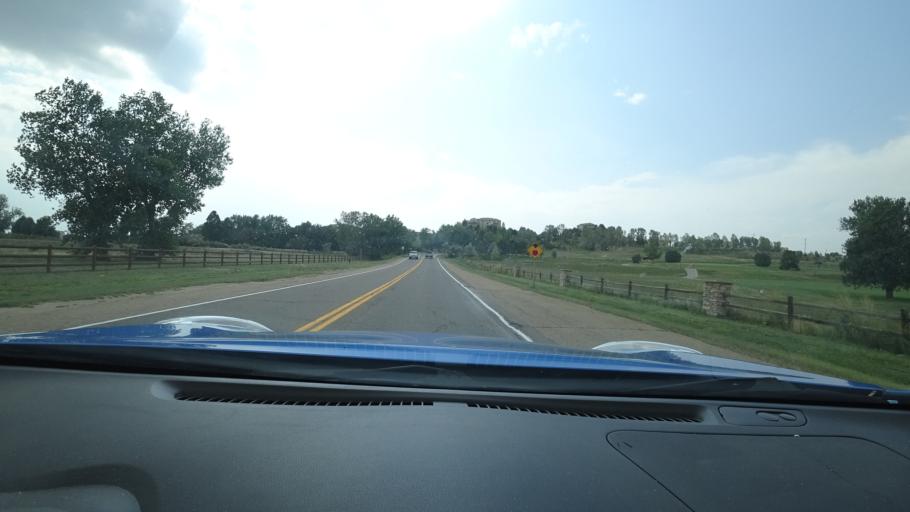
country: US
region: Colorado
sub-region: Adams County
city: Todd Creek
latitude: 39.9251
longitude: -104.8812
